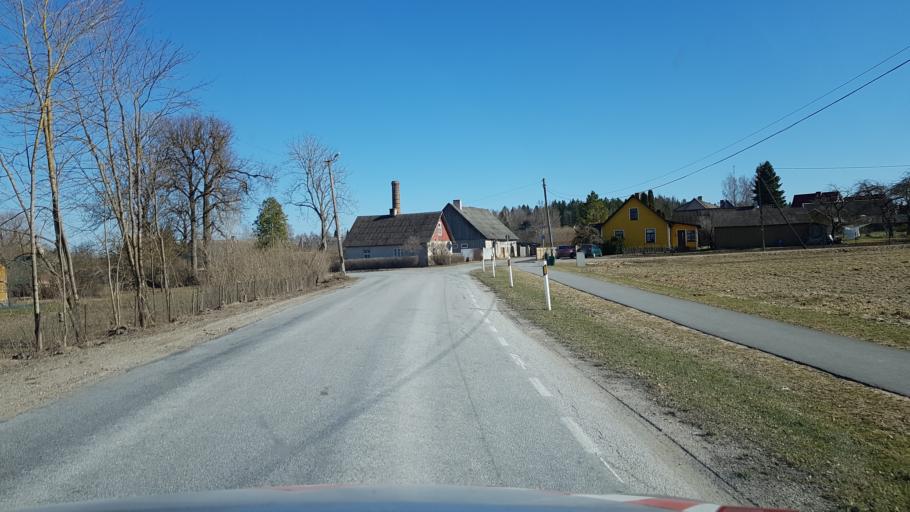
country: EE
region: Laeaene-Virumaa
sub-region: Rakke vald
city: Rakke
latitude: 58.9852
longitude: 26.2516
